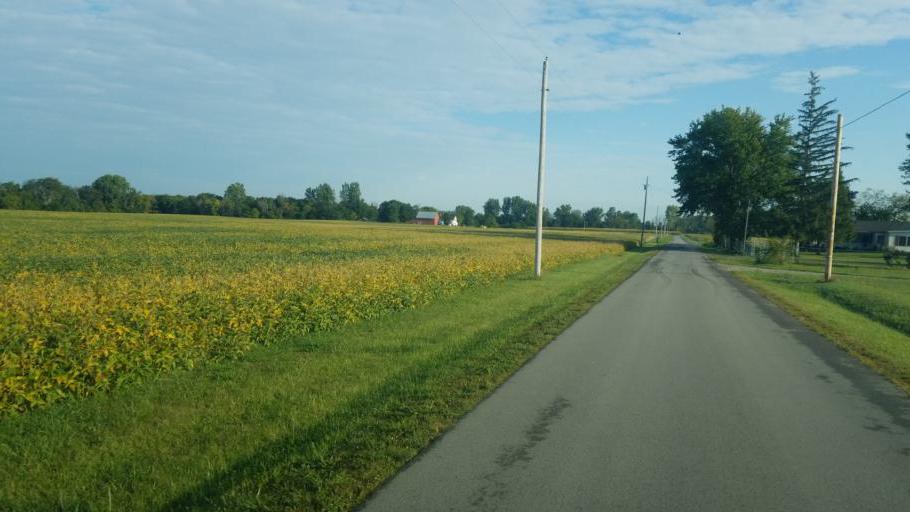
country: US
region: Ohio
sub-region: Morrow County
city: Cardington
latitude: 40.6115
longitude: -82.9380
